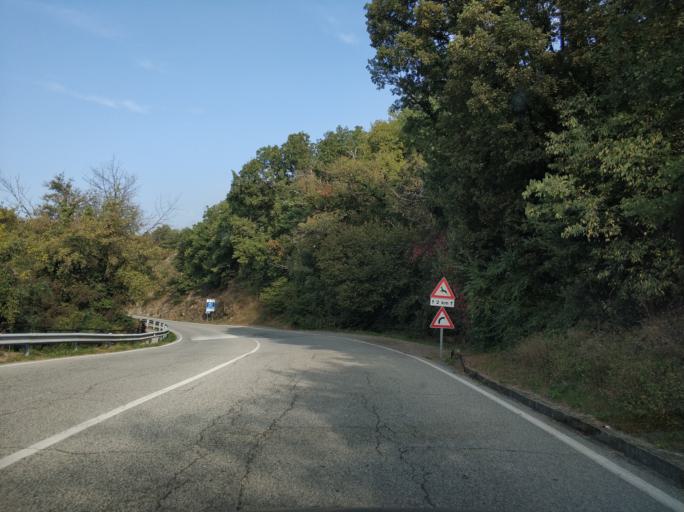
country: IT
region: Piedmont
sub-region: Provincia di Torino
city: Cascinette d'Ivrea
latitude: 45.4860
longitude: 7.8879
